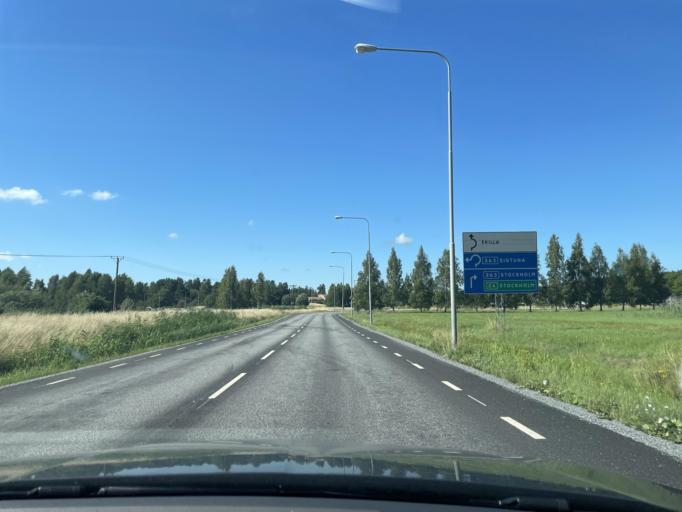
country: SE
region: Stockholm
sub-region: Sigtuna Kommun
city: Marsta
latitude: 59.6247
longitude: 17.8235
